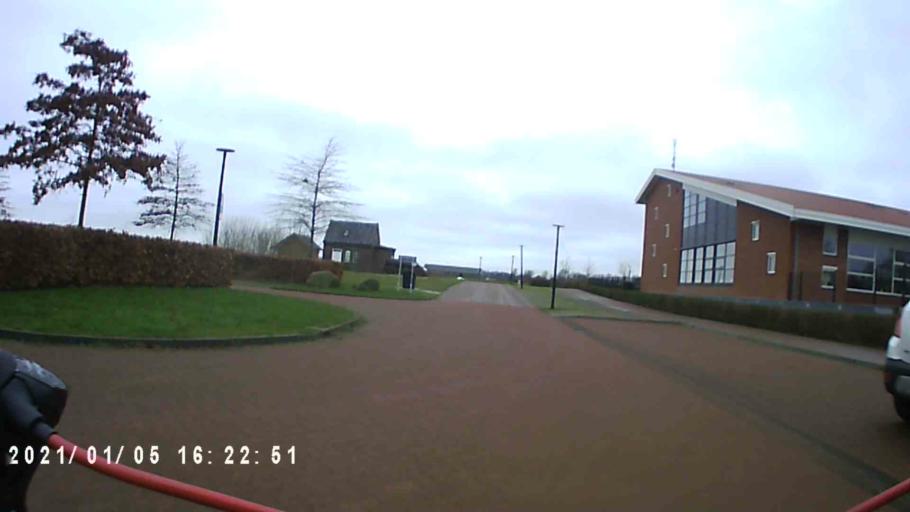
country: NL
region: Groningen
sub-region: Gemeente  Oldambt
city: Winschoten
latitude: 53.1992
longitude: 7.0383
